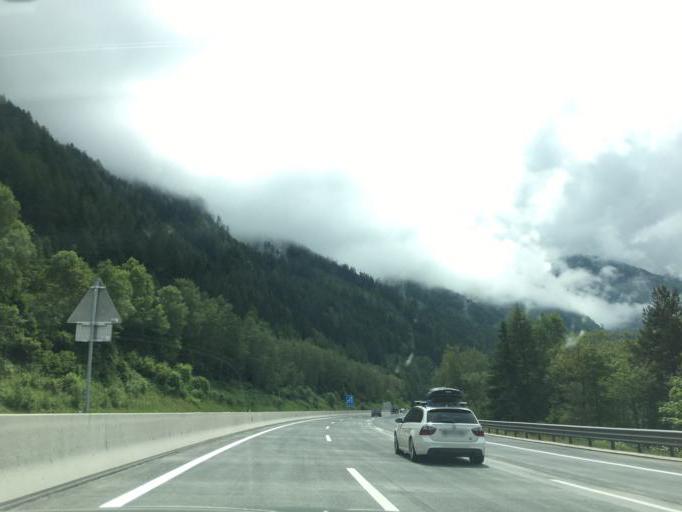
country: AT
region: Salzburg
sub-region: Politischer Bezirk Tamsweg
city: Sankt Michael im Lungau
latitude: 47.0852
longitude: 13.6061
